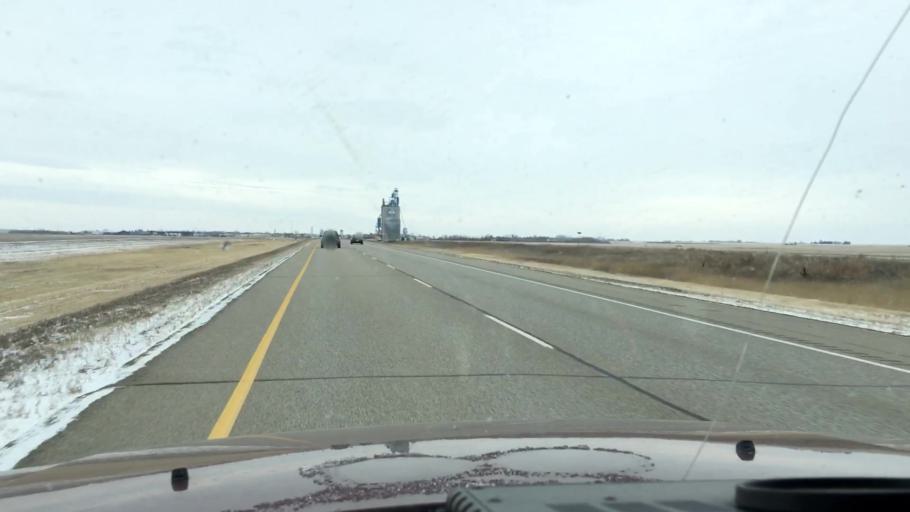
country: CA
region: Saskatchewan
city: Watrous
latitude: 51.2873
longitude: -106.0250
